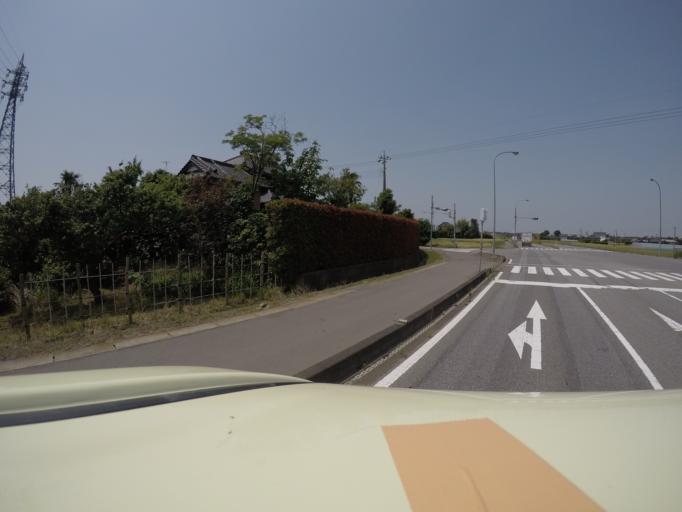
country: JP
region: Ibaraki
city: Mitsukaido
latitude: 36.0372
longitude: 139.9988
